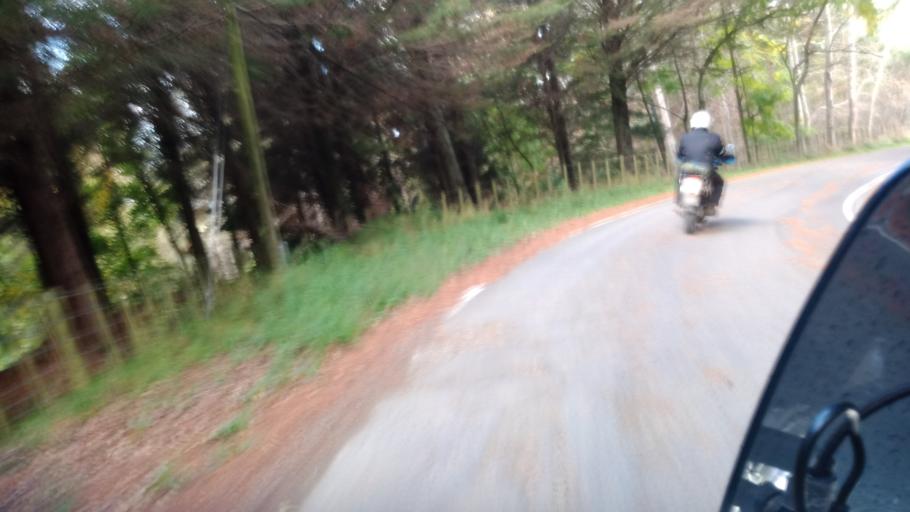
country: NZ
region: Gisborne
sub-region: Gisborne District
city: Gisborne
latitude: -38.4585
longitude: 177.6426
